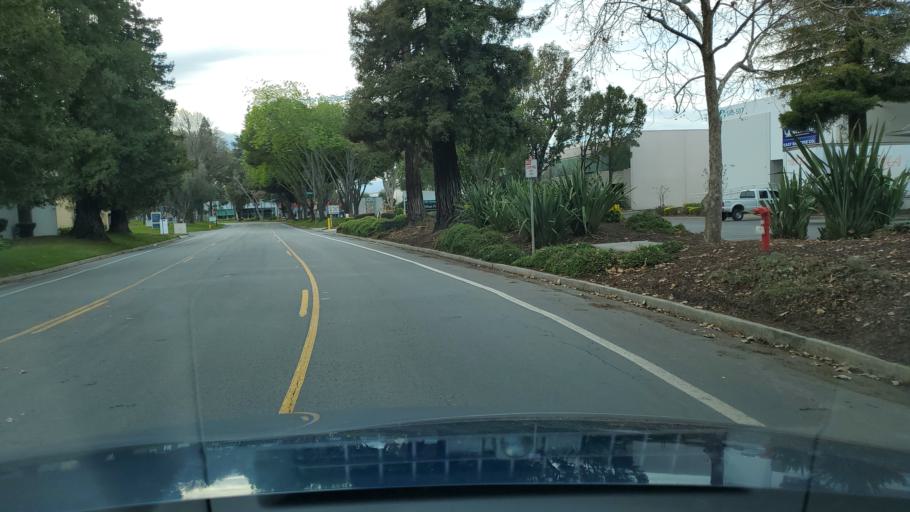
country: US
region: California
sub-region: Santa Clara County
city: Milpitas
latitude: 37.3856
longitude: -121.9103
